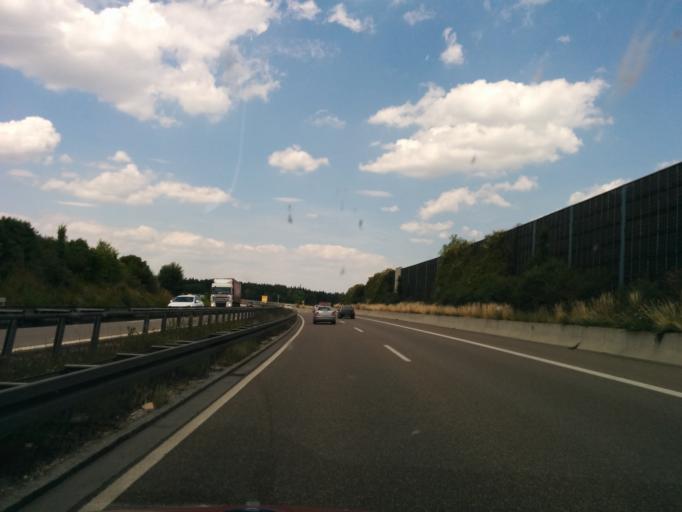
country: DE
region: Bavaria
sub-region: Swabia
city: Langweid
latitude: 48.4989
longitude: 10.8601
